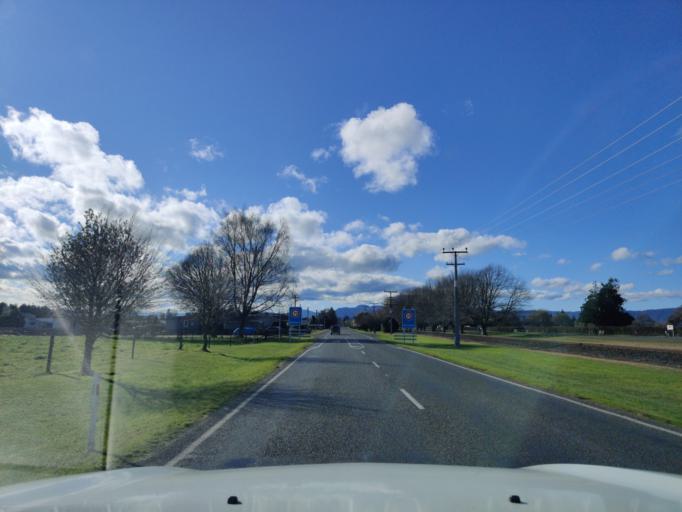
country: NZ
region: Waikato
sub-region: Matamata-Piako District
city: Matamata
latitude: -37.8302
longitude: 175.7679
